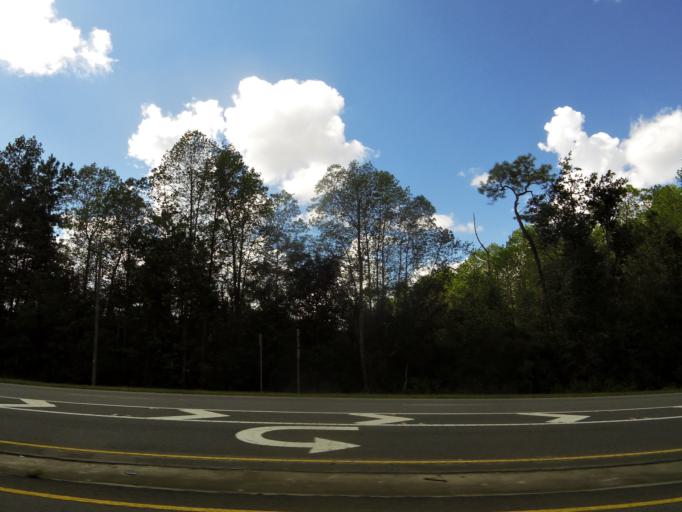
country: US
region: Georgia
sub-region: Charlton County
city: Folkston
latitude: 30.8456
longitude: -82.0075
